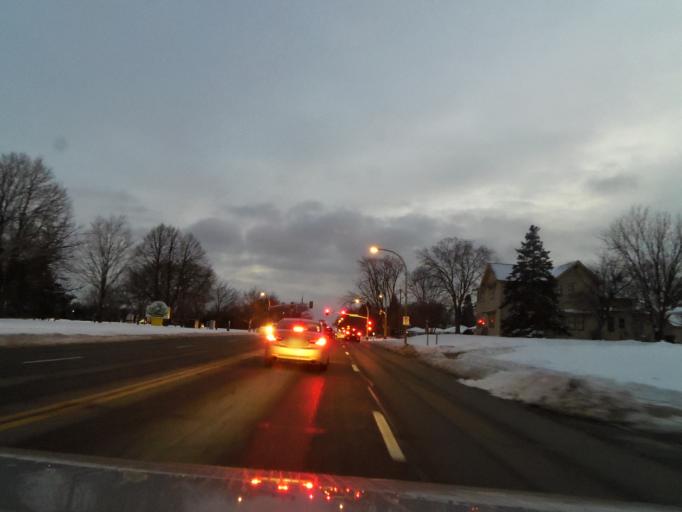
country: US
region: Minnesota
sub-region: Hennepin County
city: Richfield
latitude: 44.8881
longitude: -93.2679
